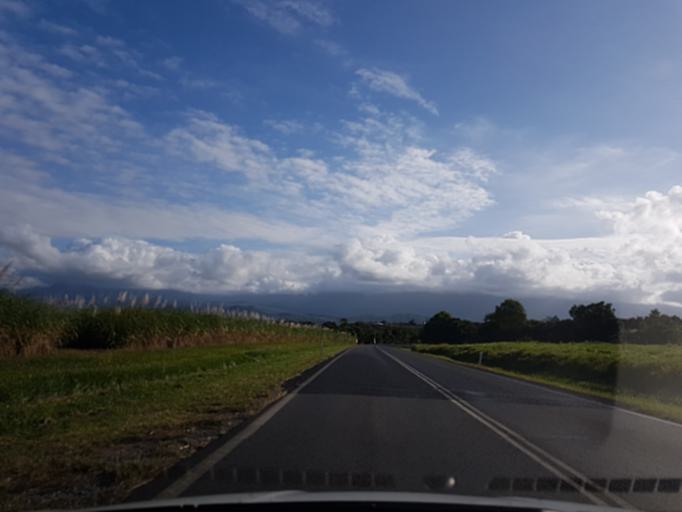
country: AU
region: Queensland
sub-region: Cairns
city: Port Douglas
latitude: -16.3926
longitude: 145.4105
